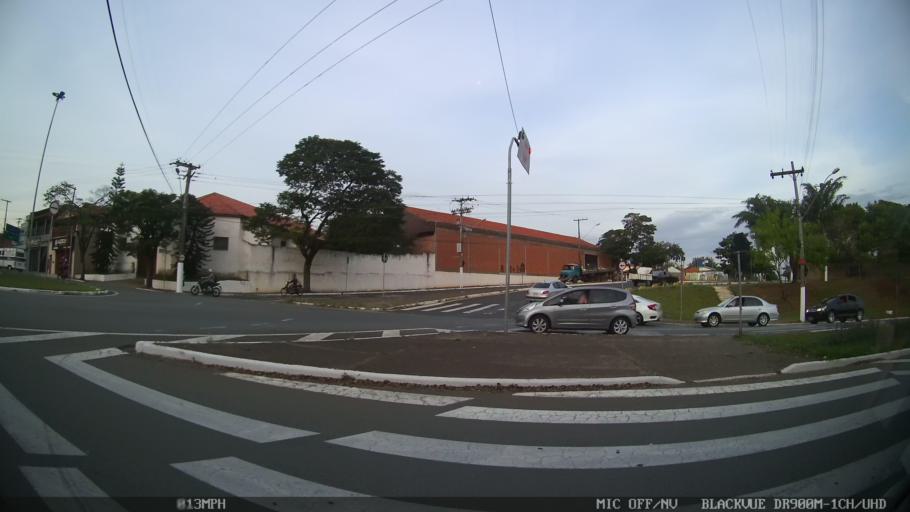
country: BR
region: Sao Paulo
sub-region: Limeira
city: Limeira
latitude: -22.5783
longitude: -47.4086
